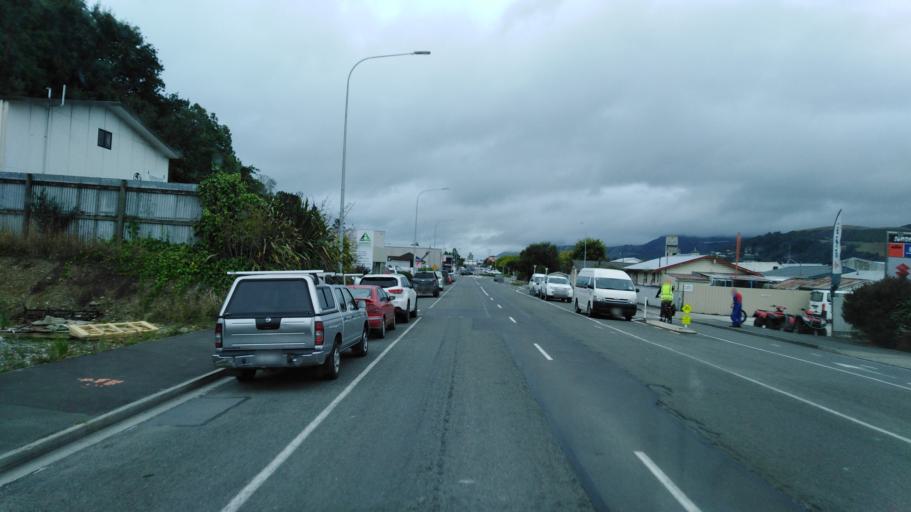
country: NZ
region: Nelson
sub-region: Nelson City
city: Nelson
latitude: -41.2752
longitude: 173.2747
